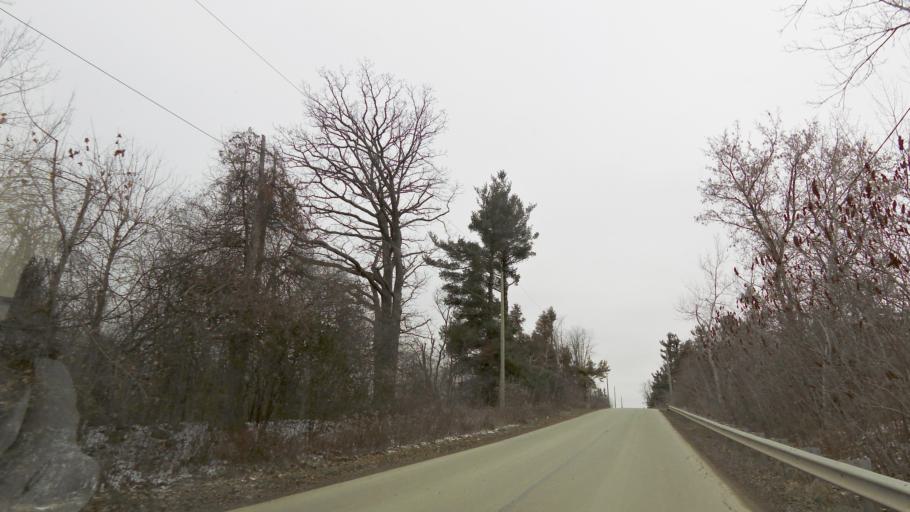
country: CA
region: Ontario
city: Vaughan
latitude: 43.8554
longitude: -79.6151
